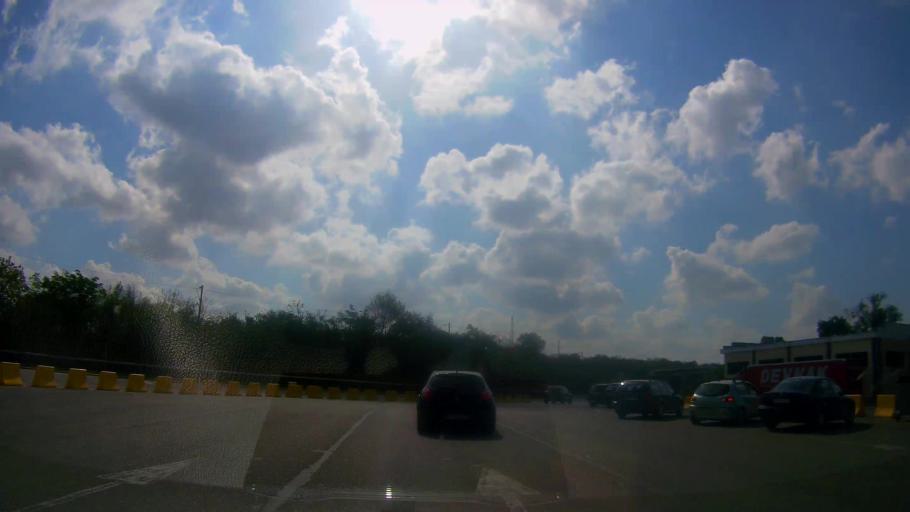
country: RO
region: Giurgiu
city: Giurgiu
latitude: 43.8787
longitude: 26.0174
